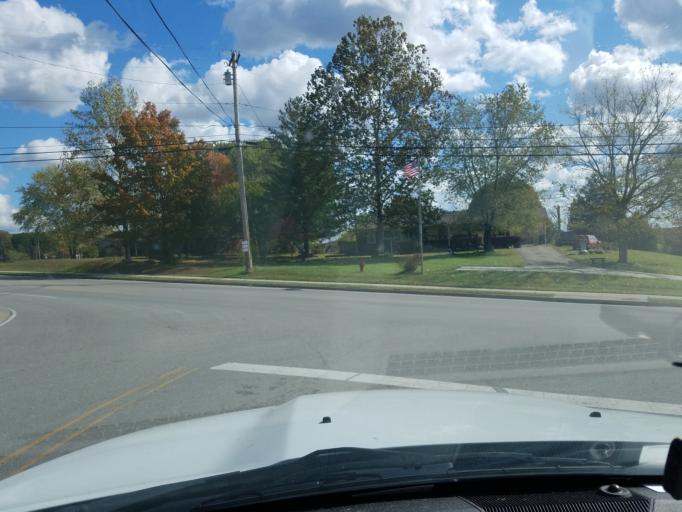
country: US
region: Kentucky
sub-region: Butler County
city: Morgantown
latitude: 37.2185
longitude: -86.6939
